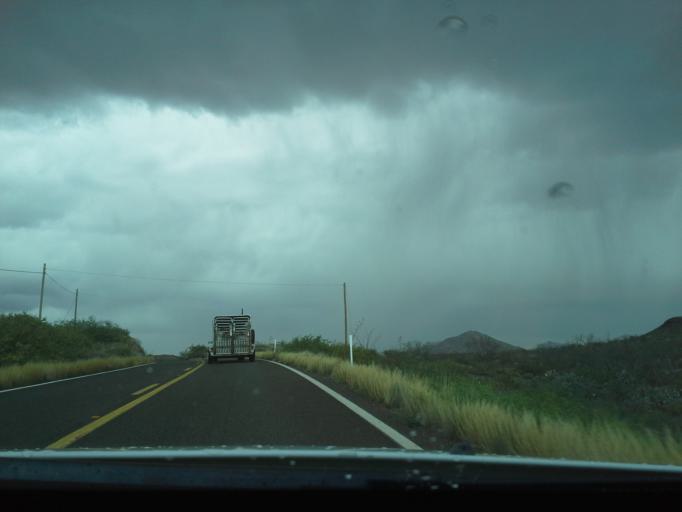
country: US
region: Arizona
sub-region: Cochise County
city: Douglas
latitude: 31.4687
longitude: -109.3851
